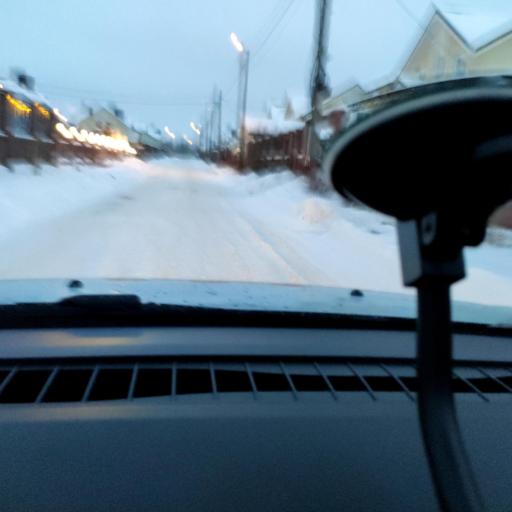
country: RU
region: Samara
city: Kurumoch
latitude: 53.4736
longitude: 50.0092
